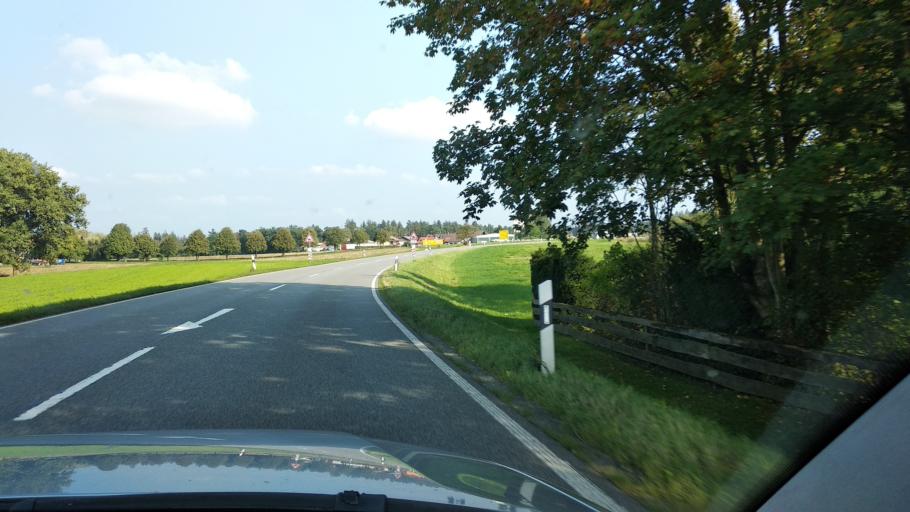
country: DE
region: Bavaria
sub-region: Upper Bavaria
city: Pfaffing
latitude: 48.0846
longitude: 12.0856
